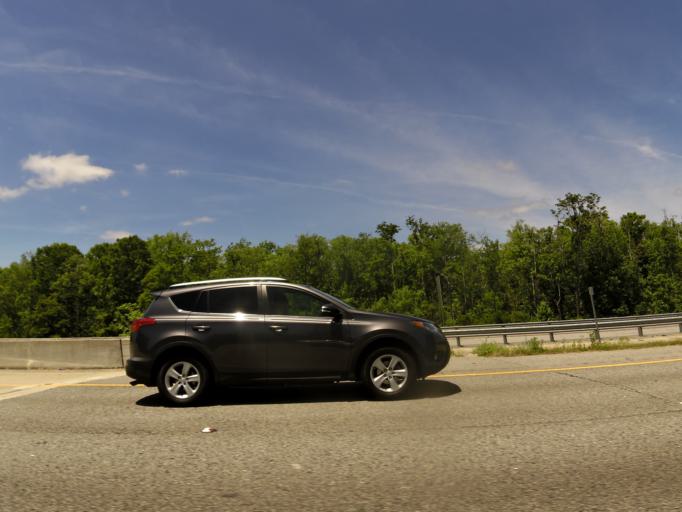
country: US
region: Georgia
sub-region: McIntosh County
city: Darien
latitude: 31.3676
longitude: -81.4564
